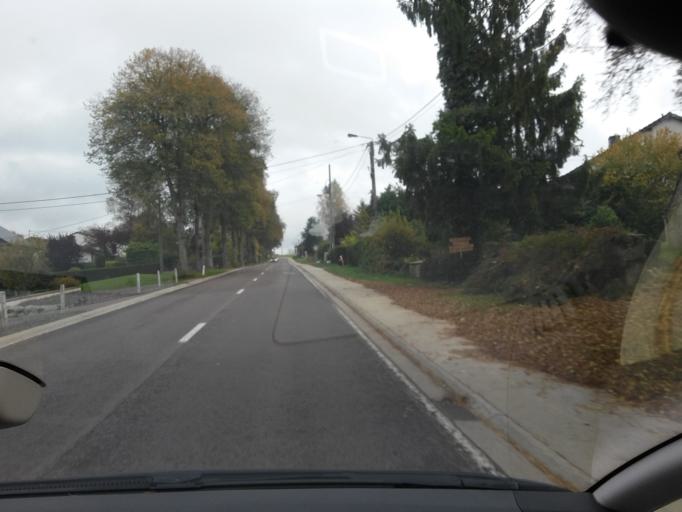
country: BE
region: Wallonia
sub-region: Province du Luxembourg
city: Attert
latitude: 49.6986
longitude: 5.7358
